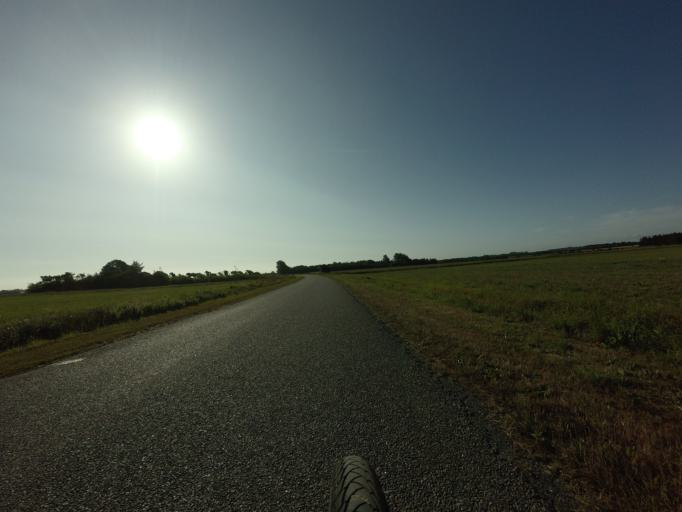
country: DK
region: North Denmark
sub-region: Hjorring Kommune
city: Vra
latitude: 57.3914
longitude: 9.9305
